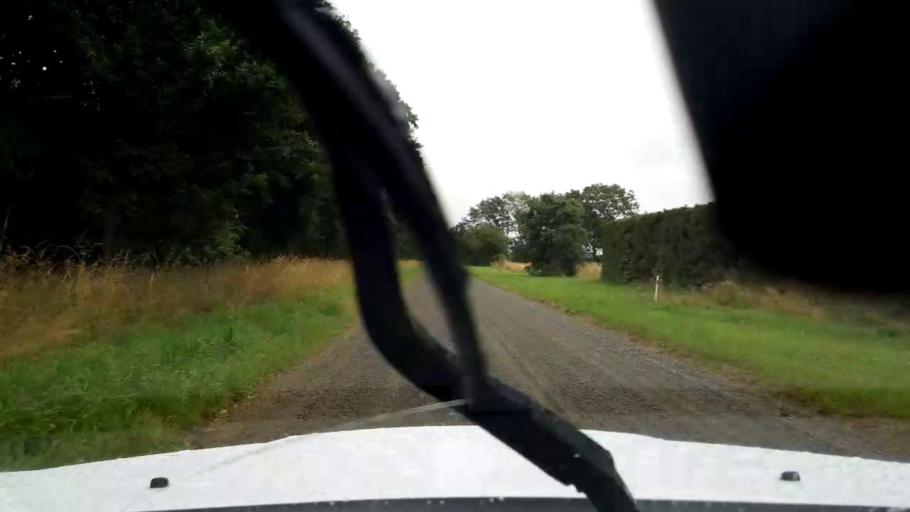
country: NZ
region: Canterbury
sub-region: Timaru District
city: Pleasant Point
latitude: -44.2189
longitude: 171.2812
